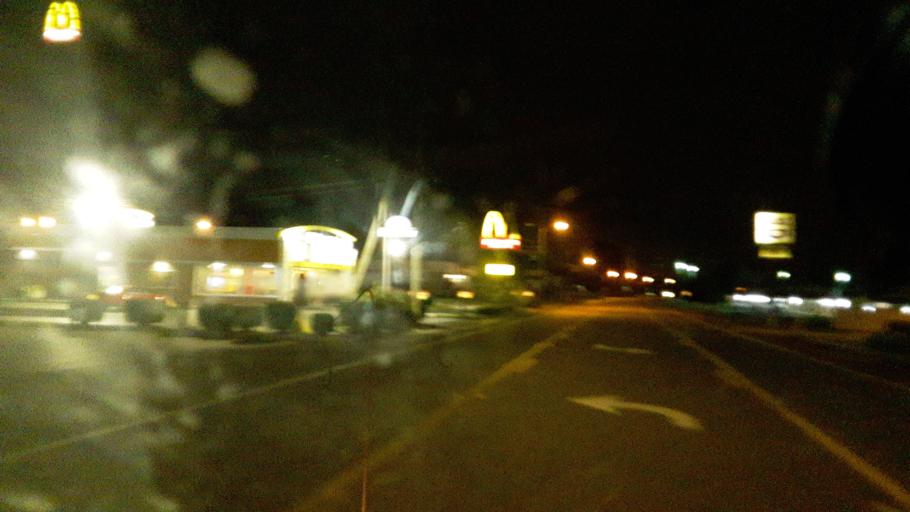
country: US
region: West Virginia
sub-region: Kanawha County
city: Rand
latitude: 38.3058
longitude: -81.5633
